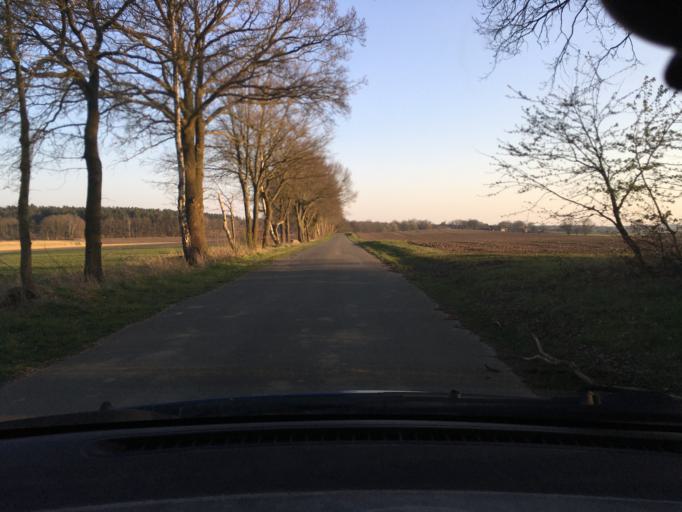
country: DE
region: Lower Saxony
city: Romstedt
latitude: 53.1603
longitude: 10.6644
